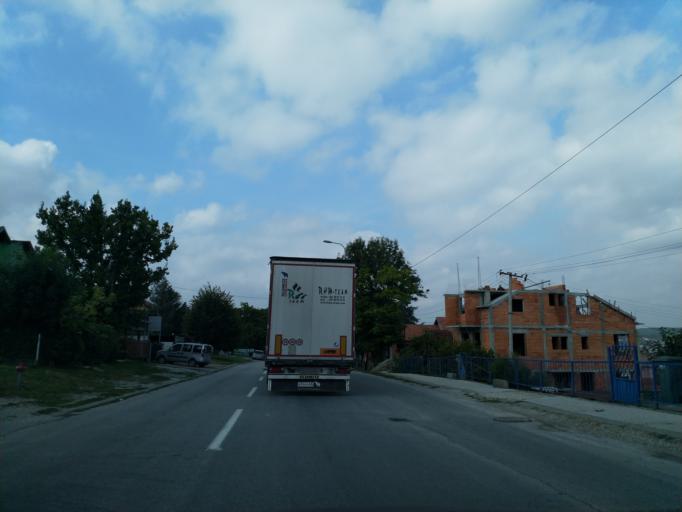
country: RS
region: Central Serbia
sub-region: Sumadijski Okrug
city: Kragujevac
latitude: 44.0320
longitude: 20.9152
